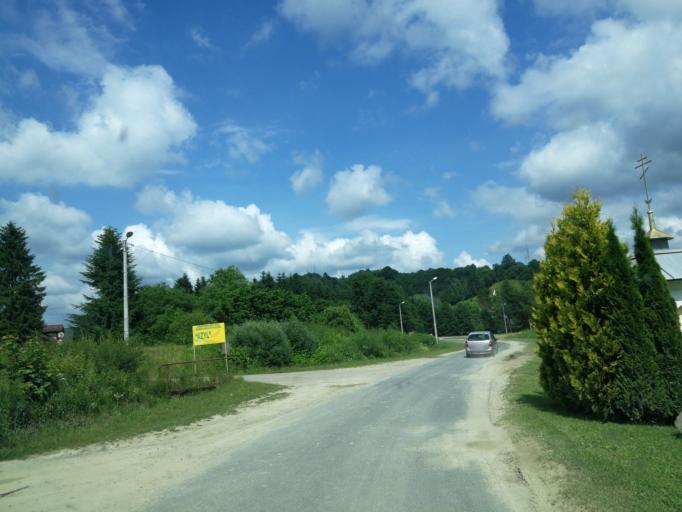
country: PL
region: Subcarpathian Voivodeship
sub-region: Powiat leski
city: Polanczyk
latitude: 49.4156
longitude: 22.4445
